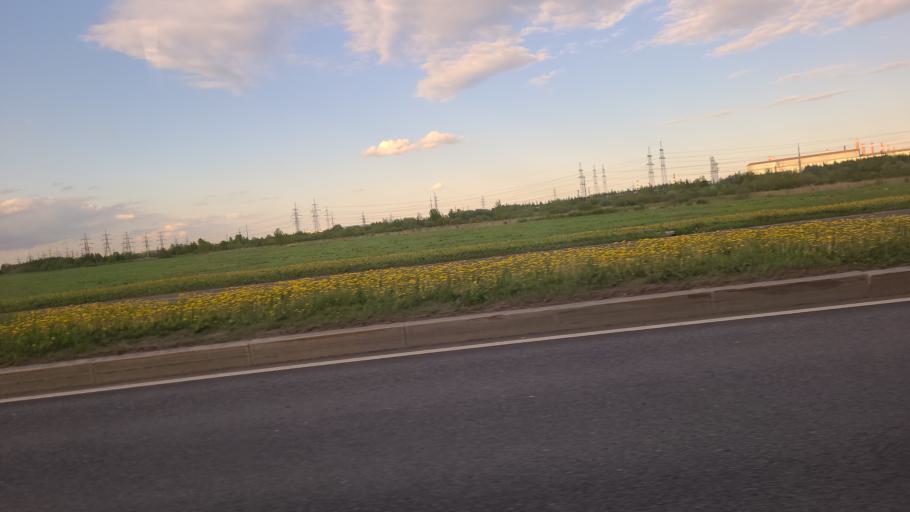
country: RU
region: St.-Petersburg
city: Petro-Slavyanka
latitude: 59.7673
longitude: 30.5016
